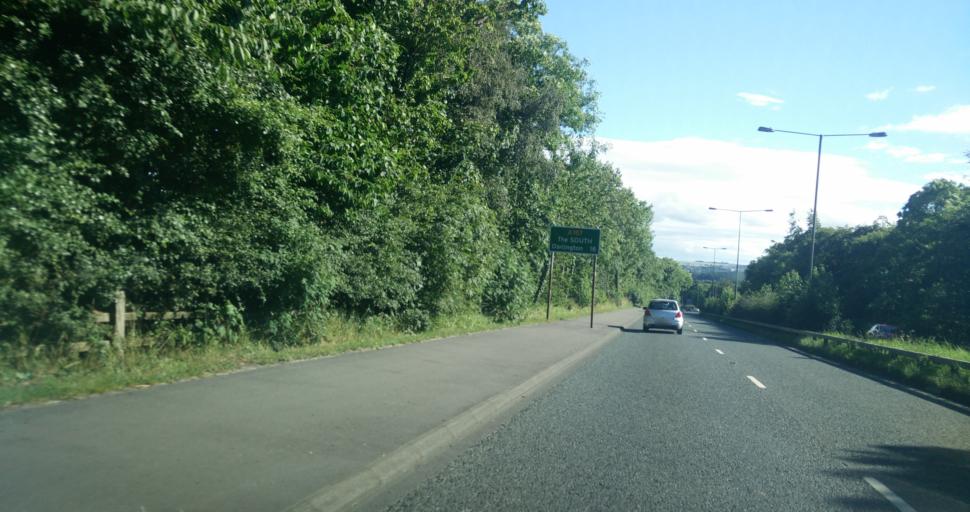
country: GB
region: England
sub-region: County Durham
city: Durham
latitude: 54.7521
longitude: -1.5906
